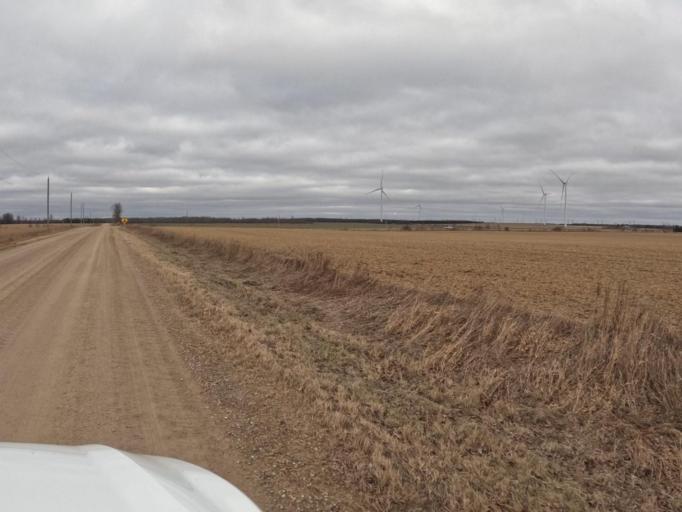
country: CA
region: Ontario
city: Shelburne
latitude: 43.8829
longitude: -80.3814
